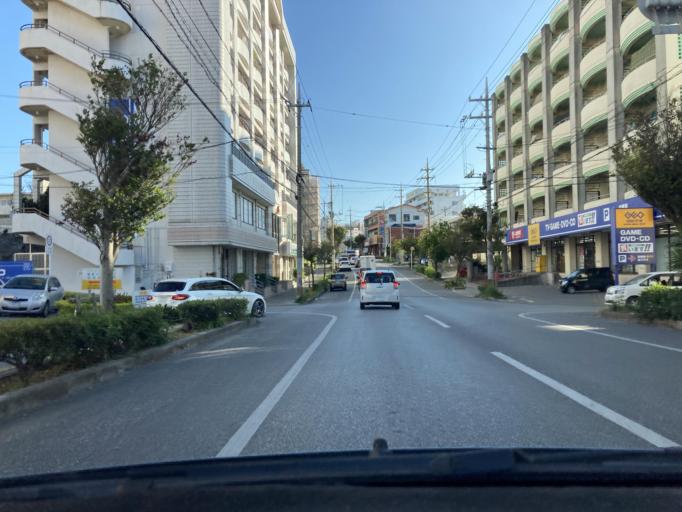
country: JP
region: Okinawa
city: Ginowan
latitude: 26.2530
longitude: 127.7140
